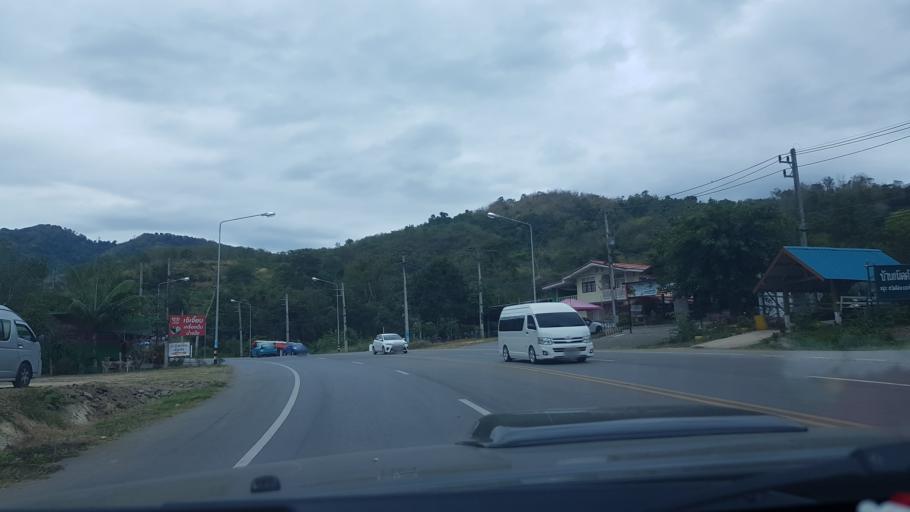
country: TH
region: Phetchabun
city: Khao Kho
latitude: 16.5437
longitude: 101.0530
